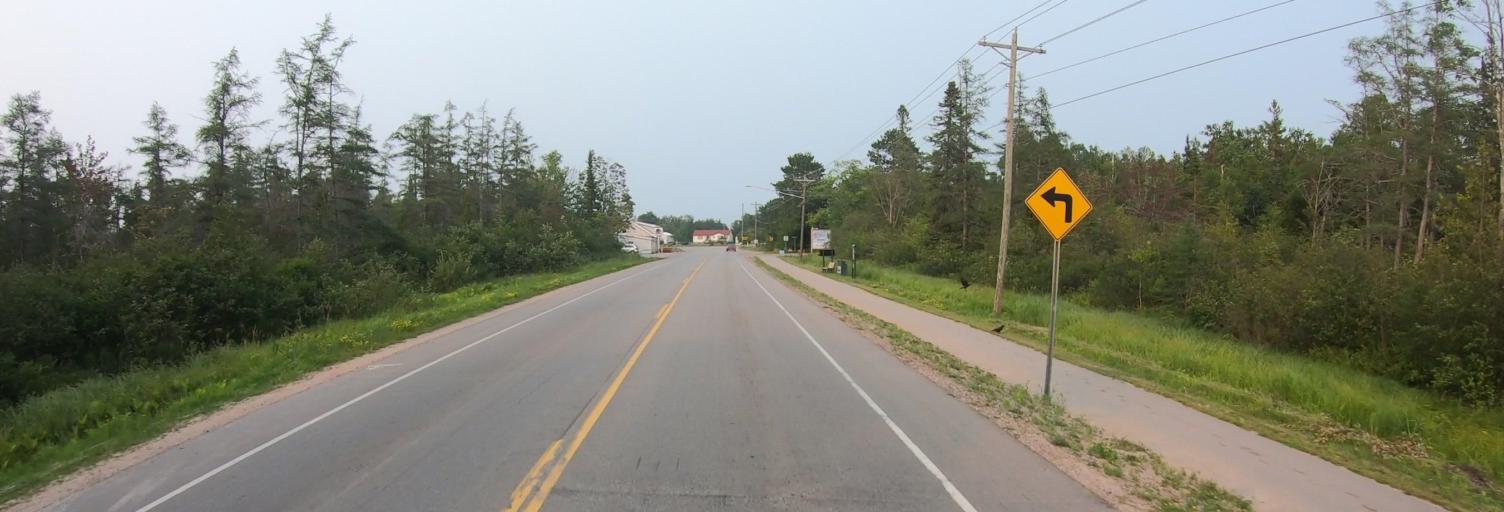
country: US
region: Michigan
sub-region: Chippewa County
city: Sault Ste. Marie
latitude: 46.4458
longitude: -84.5990
